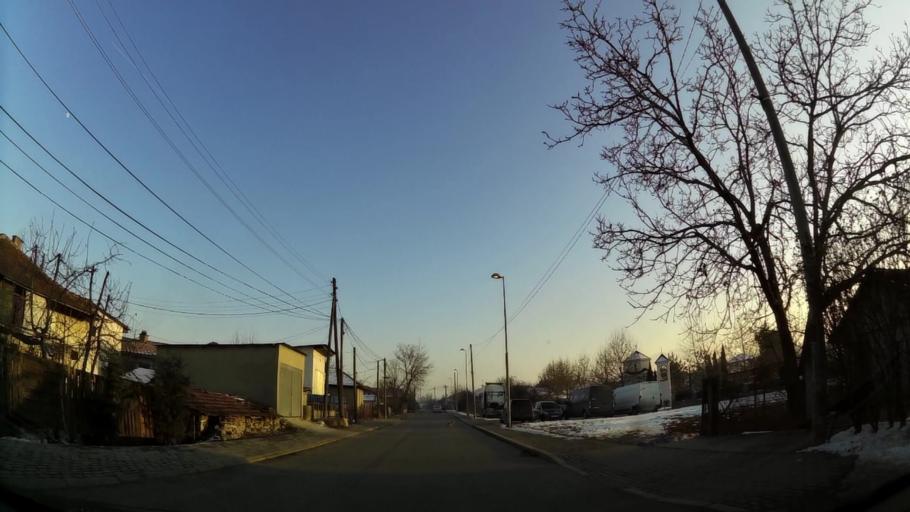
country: MK
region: Kisela Voda
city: Kisela Voda
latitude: 41.9748
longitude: 21.4867
